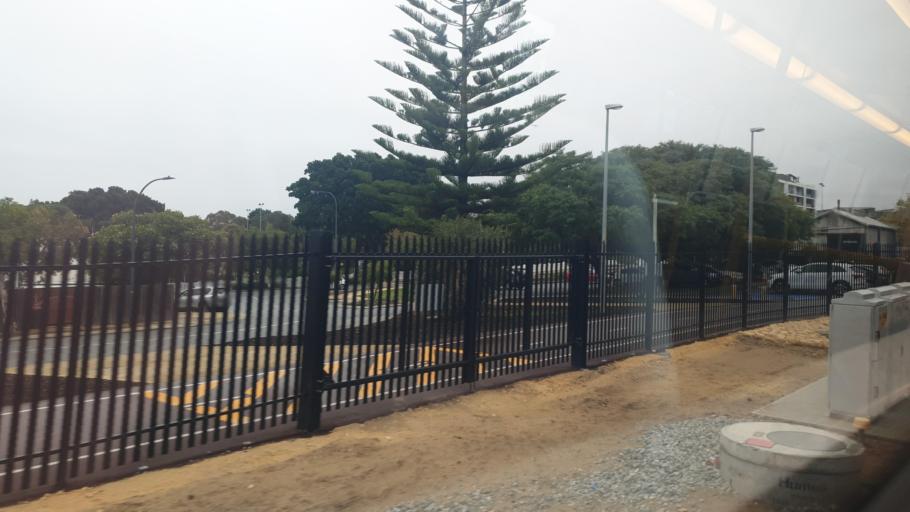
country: AU
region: Western Australia
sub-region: Claremont
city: Claremont
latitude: -31.9812
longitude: 115.7802
